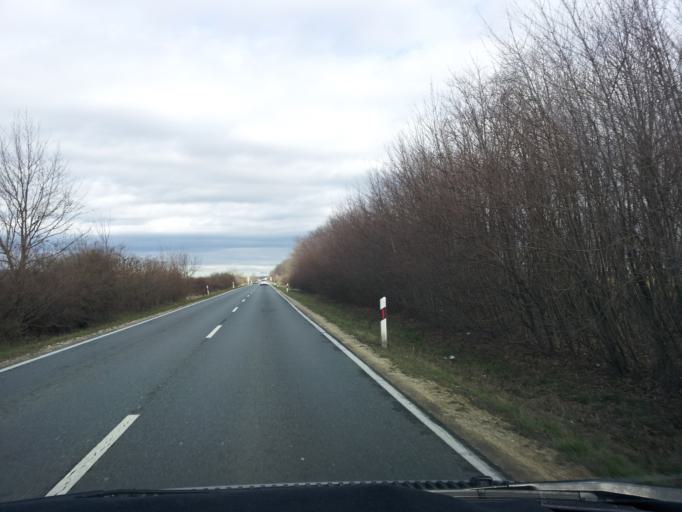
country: HU
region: Vas
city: Gencsapati
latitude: 47.2915
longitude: 16.6091
